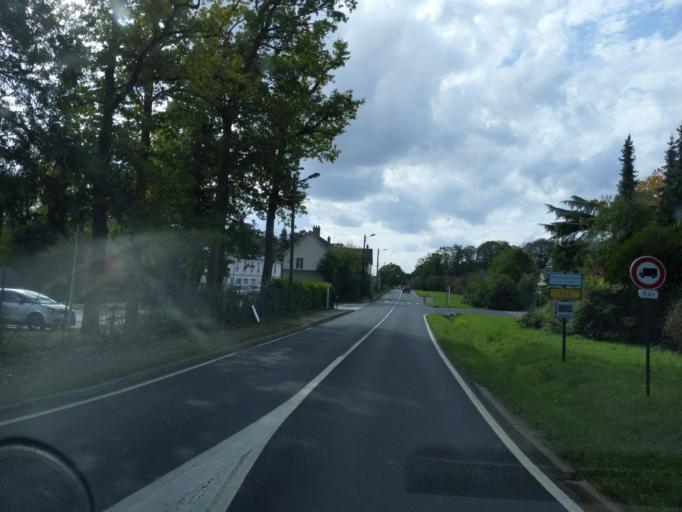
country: FR
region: Ile-de-France
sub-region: Departement des Yvelines
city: Rambouillet
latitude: 48.6508
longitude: 1.8716
